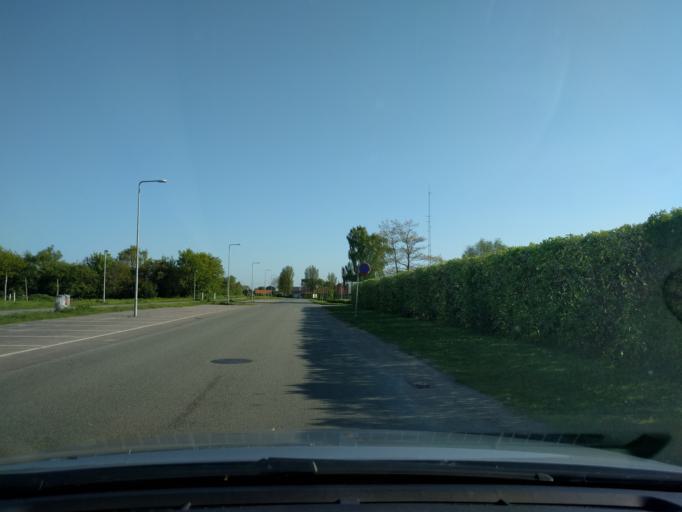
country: DK
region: South Denmark
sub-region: Kerteminde Kommune
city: Kerteminde
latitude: 55.4615
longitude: 10.6564
